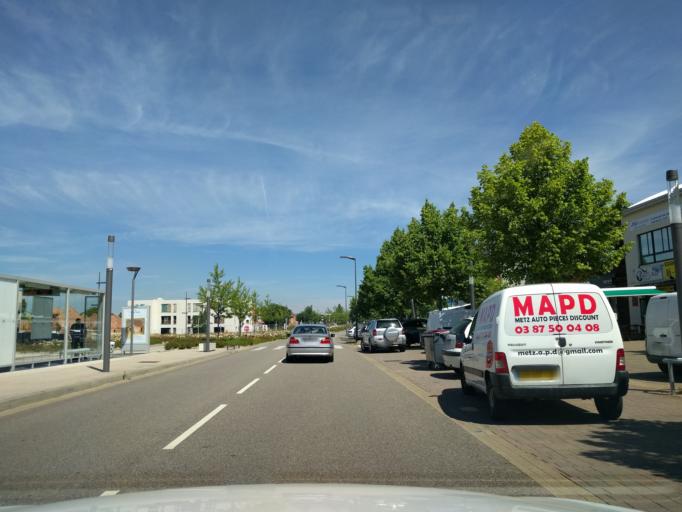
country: FR
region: Lorraine
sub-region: Departement de la Moselle
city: Saint-Julien-les-Metz
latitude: 49.1107
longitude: 6.2308
